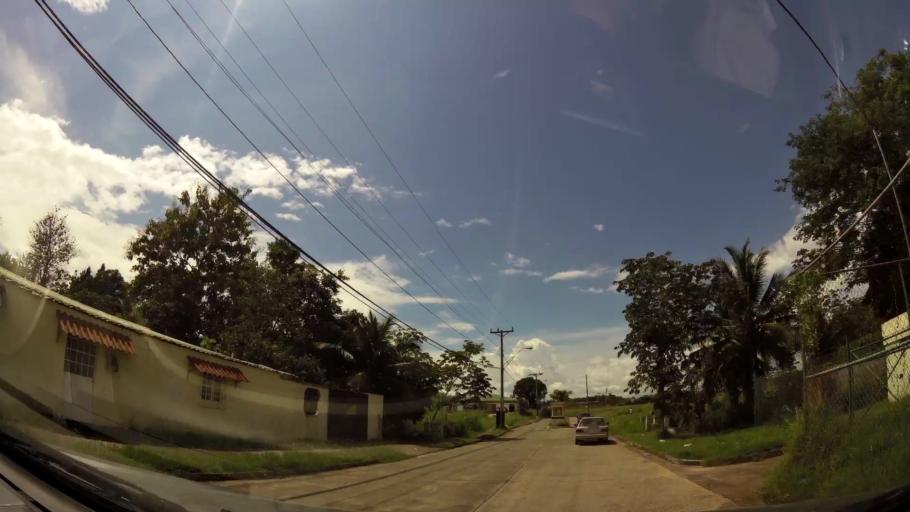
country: PA
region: Panama
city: San Vicente de Bique
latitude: 8.9198
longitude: -79.6940
